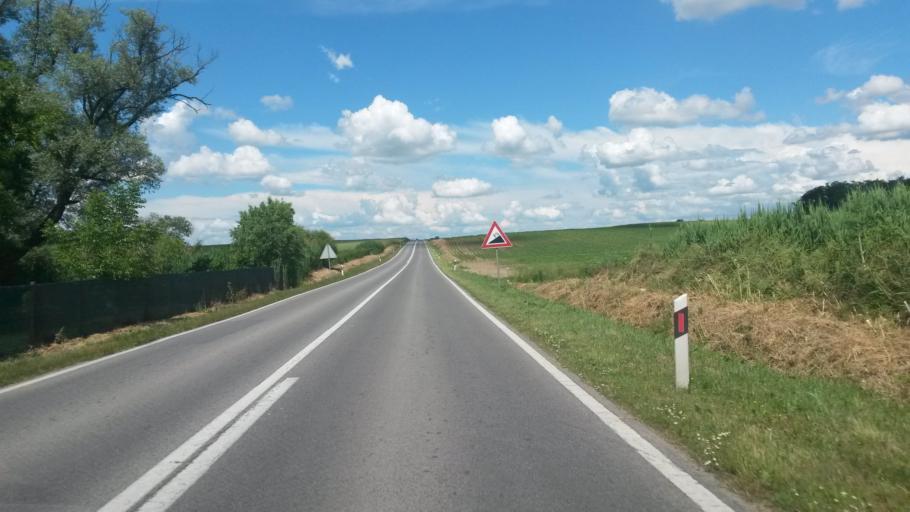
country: HR
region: Osjecko-Baranjska
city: Viskovci
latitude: 45.3701
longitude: 18.4347
